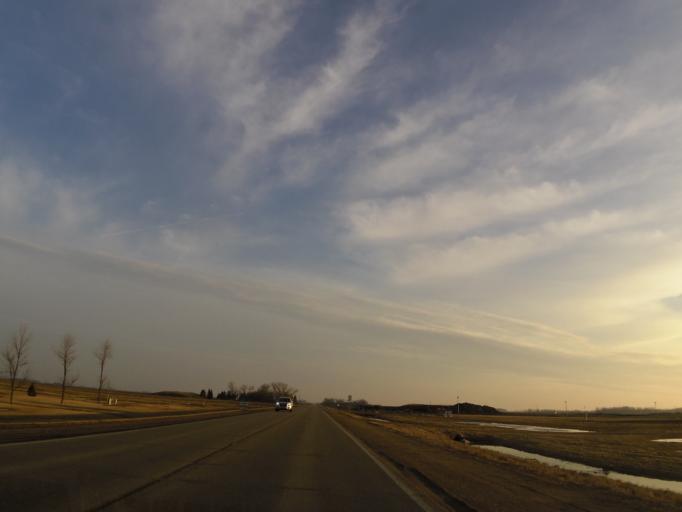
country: US
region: North Dakota
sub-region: Grand Forks County
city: Grand Forks
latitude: 47.8673
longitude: -97.0453
